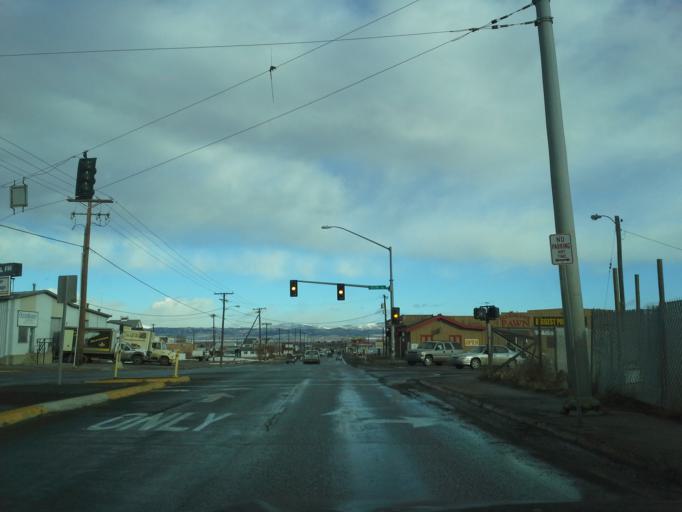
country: US
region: Montana
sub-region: Lewis and Clark County
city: Helena
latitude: 46.5978
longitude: -112.0201
